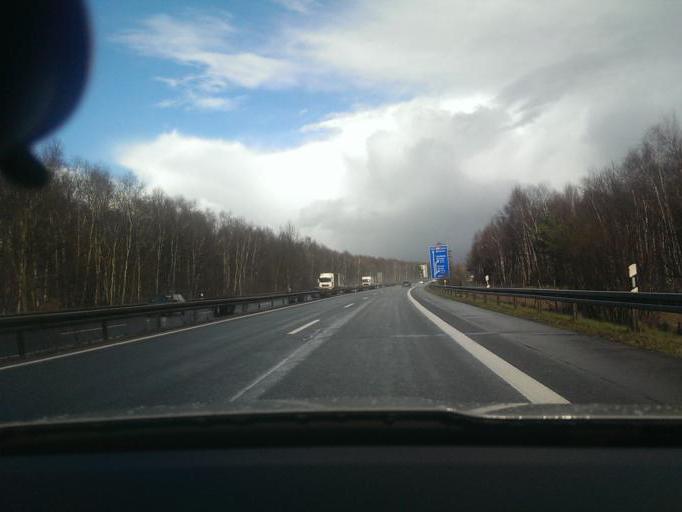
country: DE
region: Lower Saxony
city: Isernhagen Farster Bauerschaft
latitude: 52.4211
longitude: 9.8616
